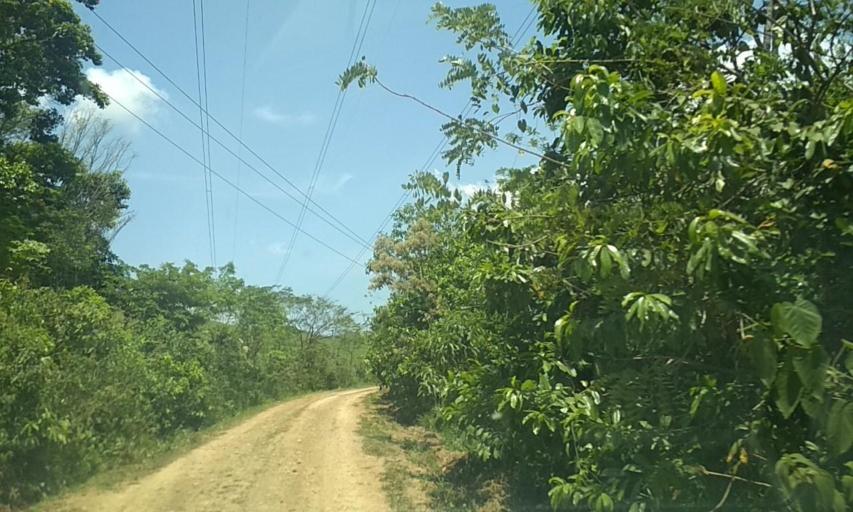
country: MX
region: Chiapas
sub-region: Tecpatan
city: Raudales Malpaso
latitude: 17.3946
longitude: -93.7411
